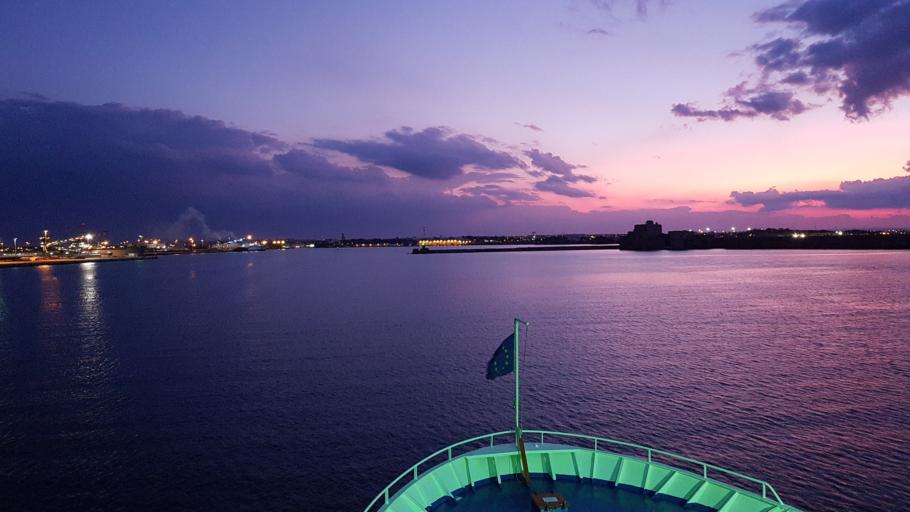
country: IT
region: Apulia
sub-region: Provincia di Brindisi
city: Materdomini
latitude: 40.6555
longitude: 17.9776
